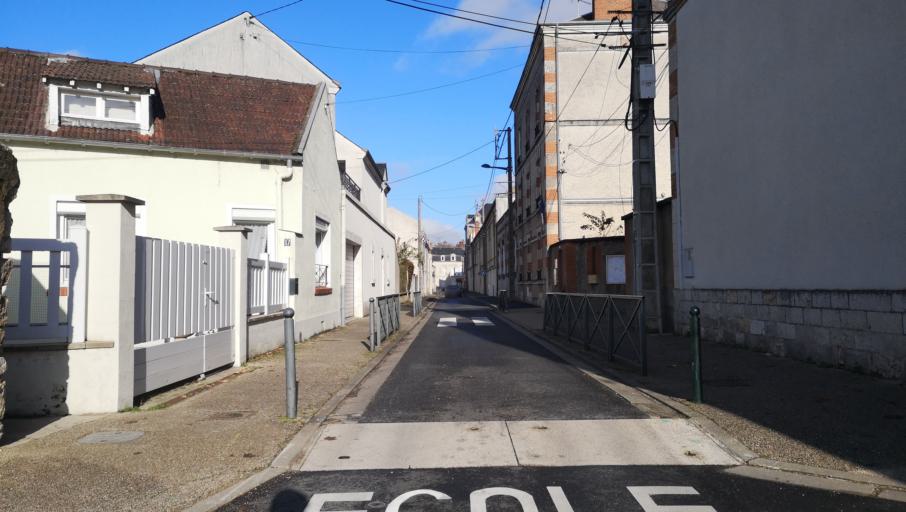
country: FR
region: Centre
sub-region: Departement du Loiret
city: Saint-Jean-le-Blanc
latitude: 47.9026
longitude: 1.9207
